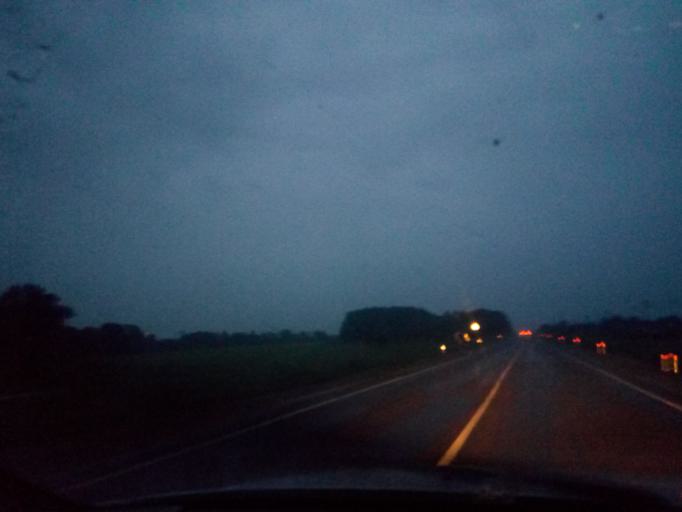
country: RU
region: Primorskiy
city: Dal'nerechensk
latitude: 45.9038
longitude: 133.7502
